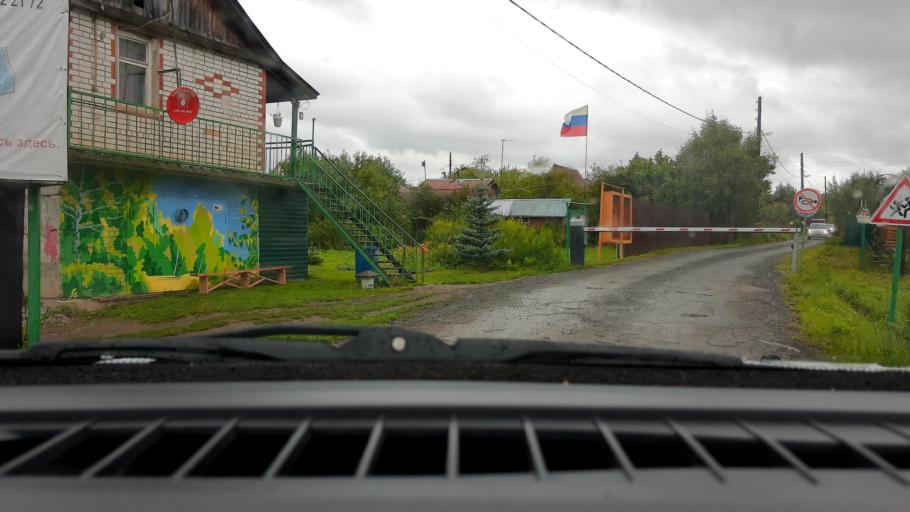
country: RU
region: Nizjnij Novgorod
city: Babino
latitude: 56.1515
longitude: 43.6361
